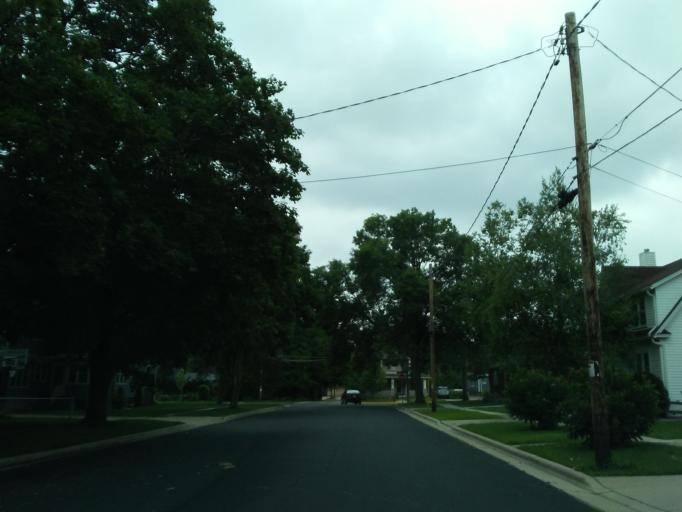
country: US
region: Wisconsin
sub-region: Dane County
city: Middleton
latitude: 43.0958
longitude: -89.5067
